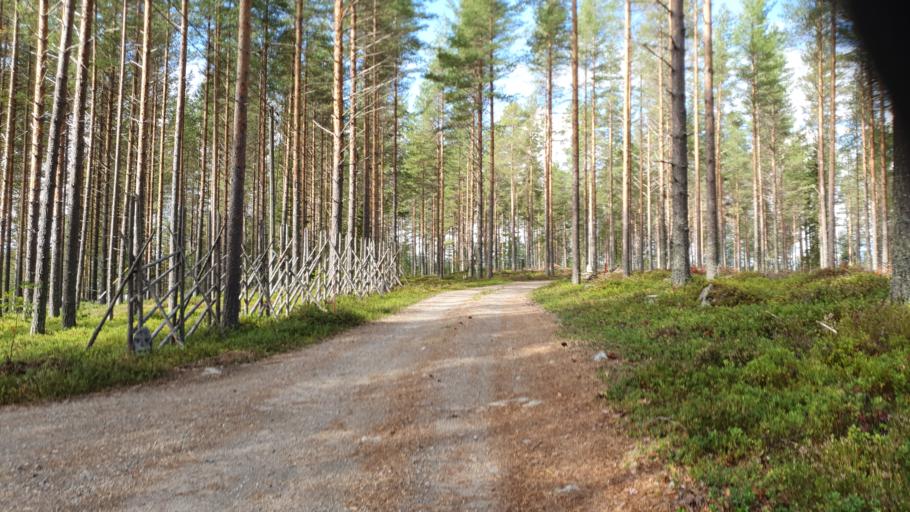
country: FI
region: Kainuu
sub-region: Kehys-Kainuu
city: Kuhmo
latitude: 64.1292
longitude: 29.3508
